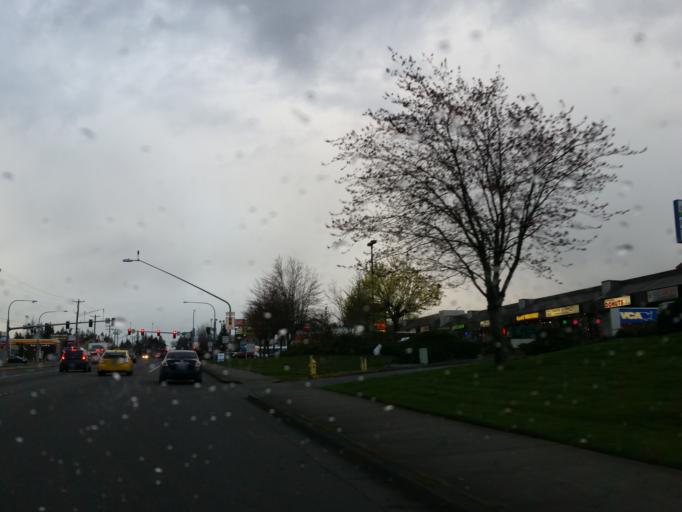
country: US
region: Washington
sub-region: Snohomish County
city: Alderwood Manor
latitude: 47.8159
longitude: -122.2922
